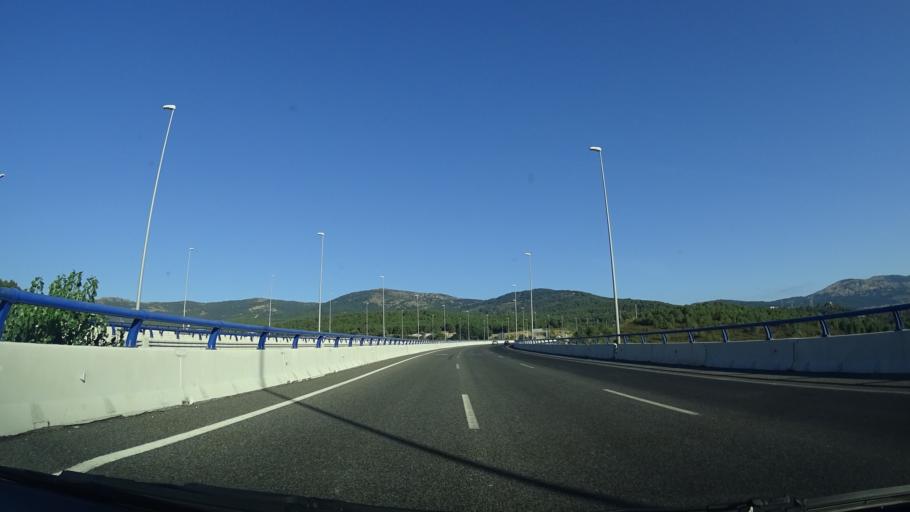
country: ES
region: Madrid
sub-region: Provincia de Madrid
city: Guadarrama
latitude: 40.6708
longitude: -4.1087
